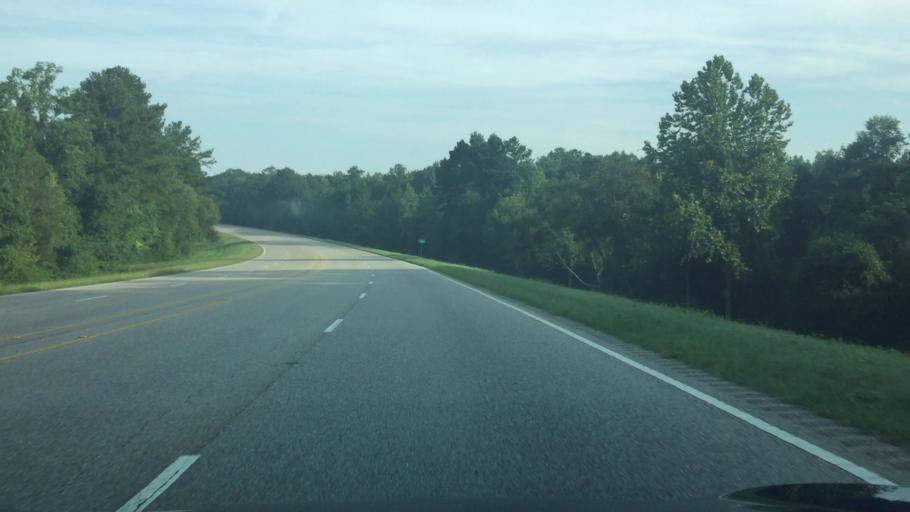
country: US
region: Alabama
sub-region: Covington County
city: Andalusia
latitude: 31.3950
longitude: -86.5742
